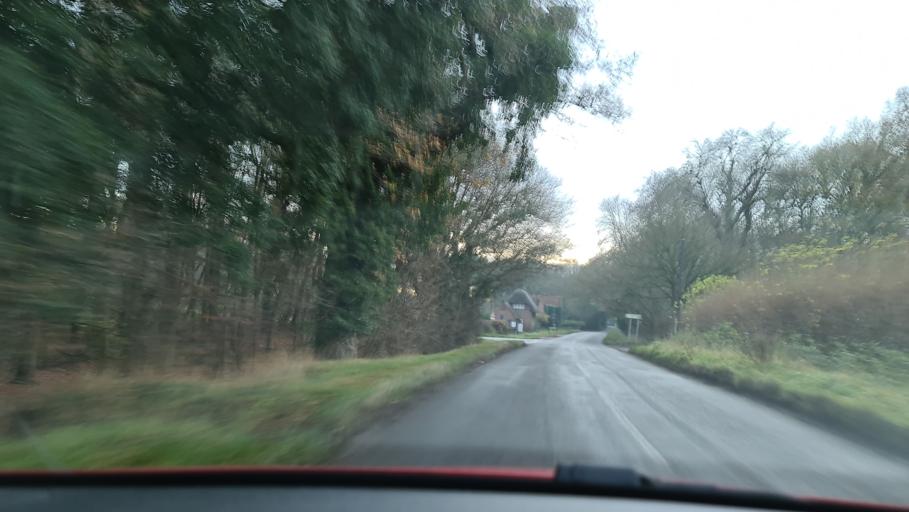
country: GB
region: England
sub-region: Buckinghamshire
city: Great Missenden
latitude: 51.7144
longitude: -0.7534
